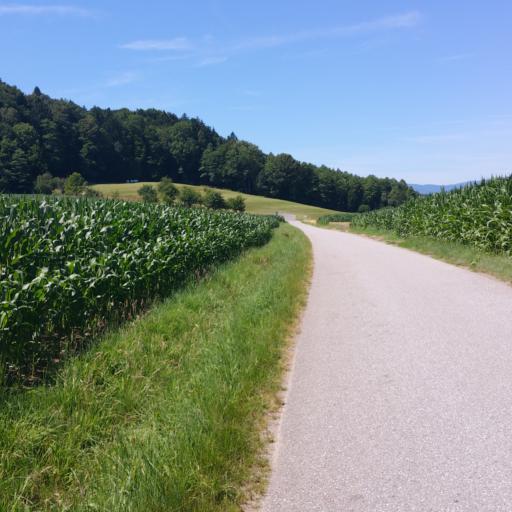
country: AT
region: Styria
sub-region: Politischer Bezirk Leibnitz
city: Gleinstatten
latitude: 46.7396
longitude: 15.3545
